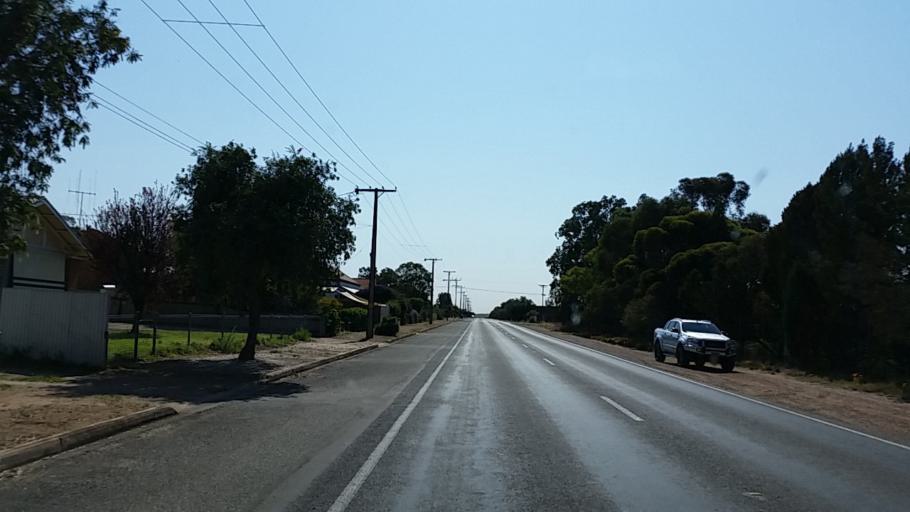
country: AU
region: South Australia
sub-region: Port Pirie City and Dists
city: Crystal Brook
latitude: -33.2627
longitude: 138.3532
